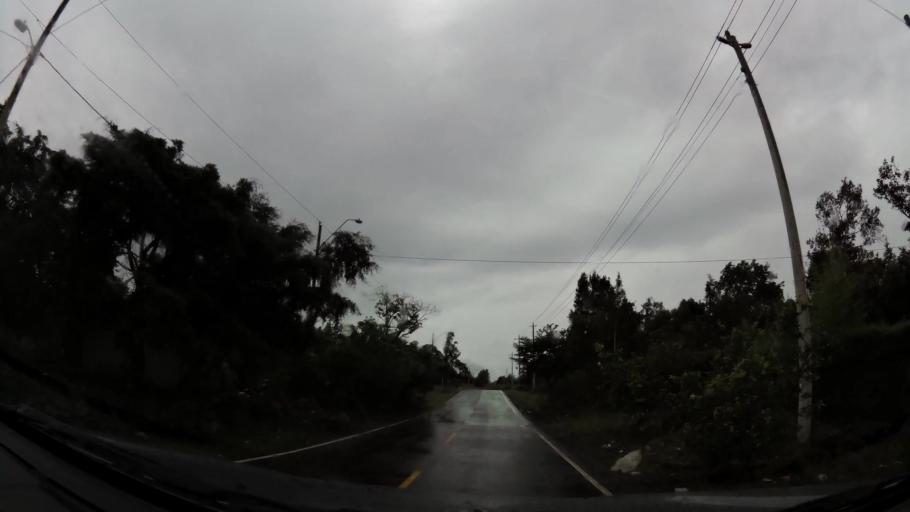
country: PA
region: Chiriqui
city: Volcan
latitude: 8.7962
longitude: -82.6469
